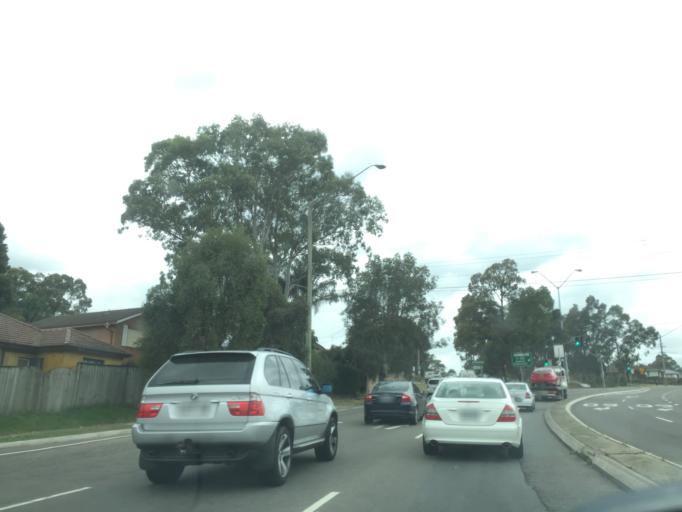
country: AU
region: New South Wales
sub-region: Blacktown
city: Blacktown
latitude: -33.7682
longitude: 150.9430
